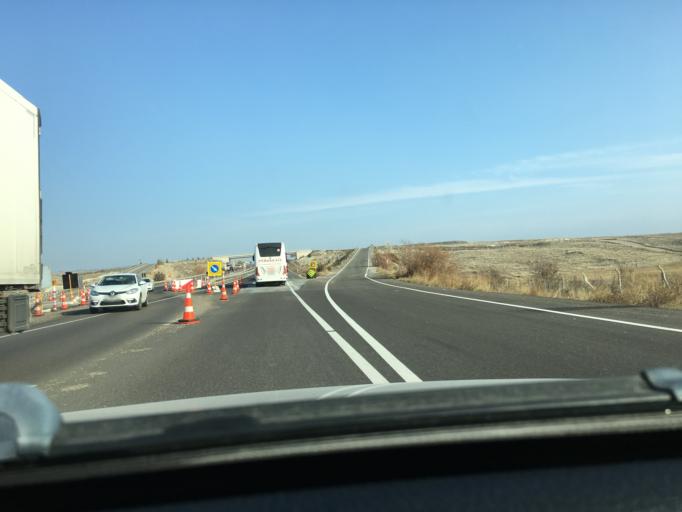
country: TR
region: Eskisehir
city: Gunyuzu
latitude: 39.5748
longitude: 31.8773
